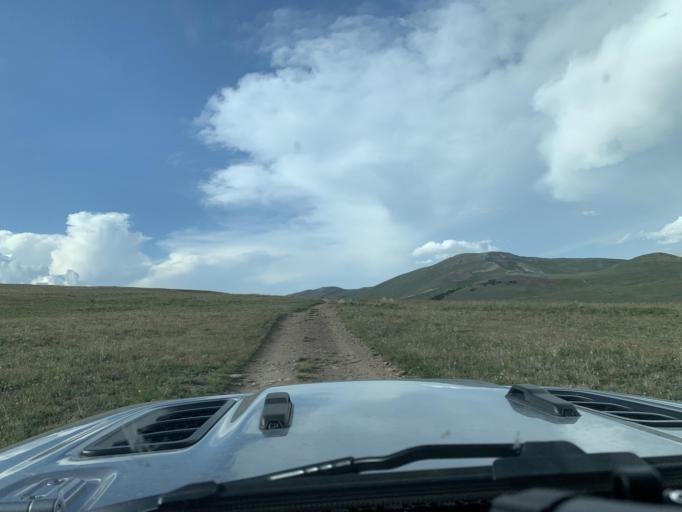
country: US
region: Colorado
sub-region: Lake County
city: Leadville North
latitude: 39.3183
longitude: -106.2732
